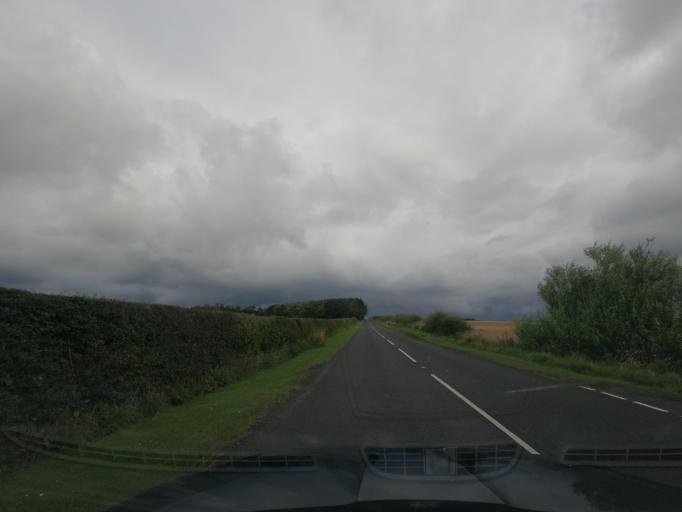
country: GB
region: England
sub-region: Northumberland
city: Ancroft
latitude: 55.7155
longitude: -1.9913
